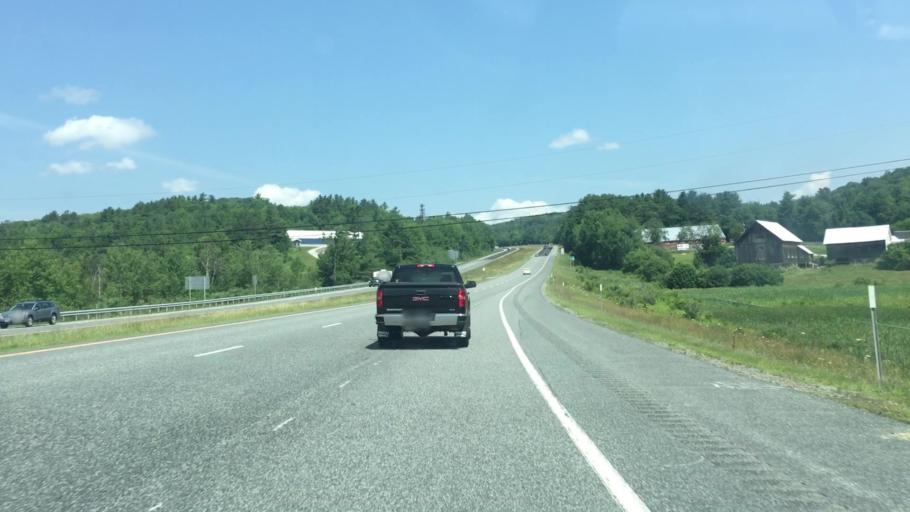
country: US
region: New Hampshire
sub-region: Sullivan County
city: Grantham
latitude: 43.5033
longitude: -72.1340
